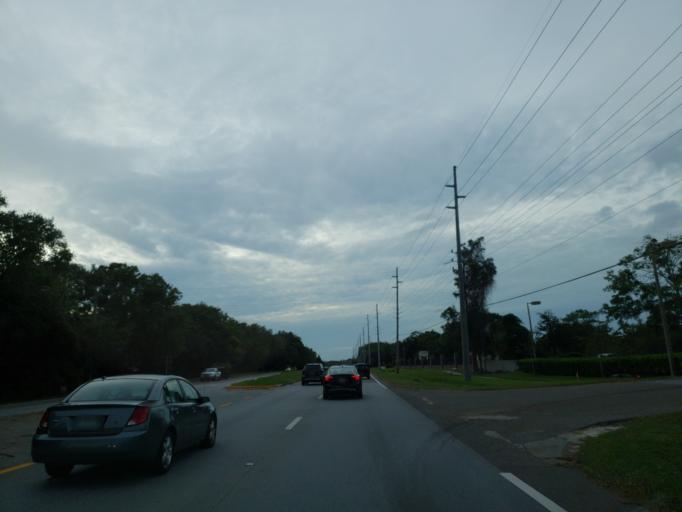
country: US
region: Florida
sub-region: Hillsborough County
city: Carrollwood Village
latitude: 28.0618
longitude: -82.5432
